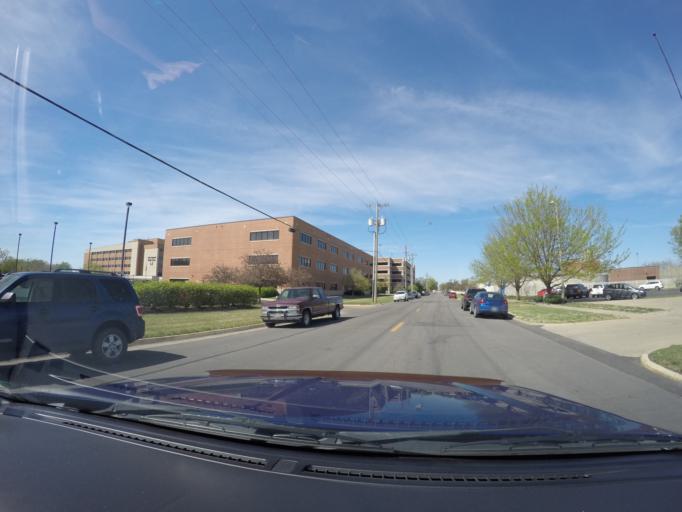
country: US
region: Kansas
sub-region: Saline County
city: Salina
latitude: 38.8318
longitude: -97.6080
